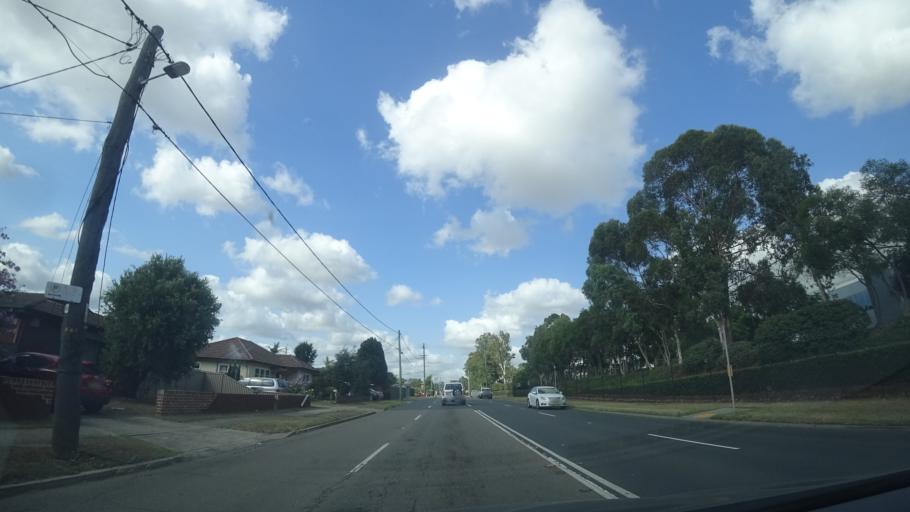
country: AU
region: New South Wales
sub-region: Fairfield
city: Liverpool
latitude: -33.9318
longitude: 150.9296
